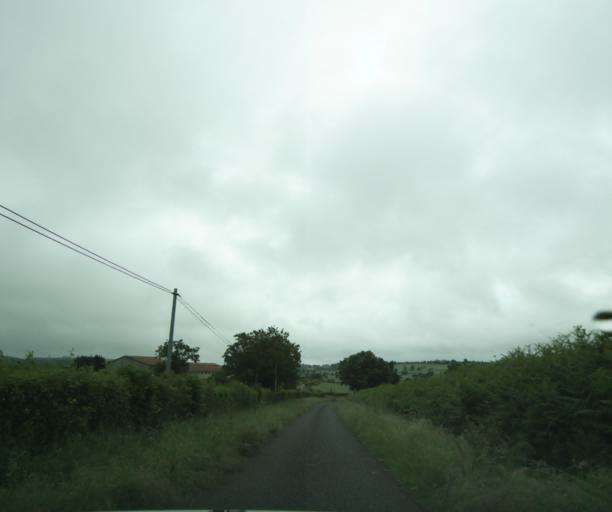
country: FR
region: Bourgogne
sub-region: Departement de Saone-et-Loire
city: La Clayette
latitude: 46.3491
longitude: 4.2310
